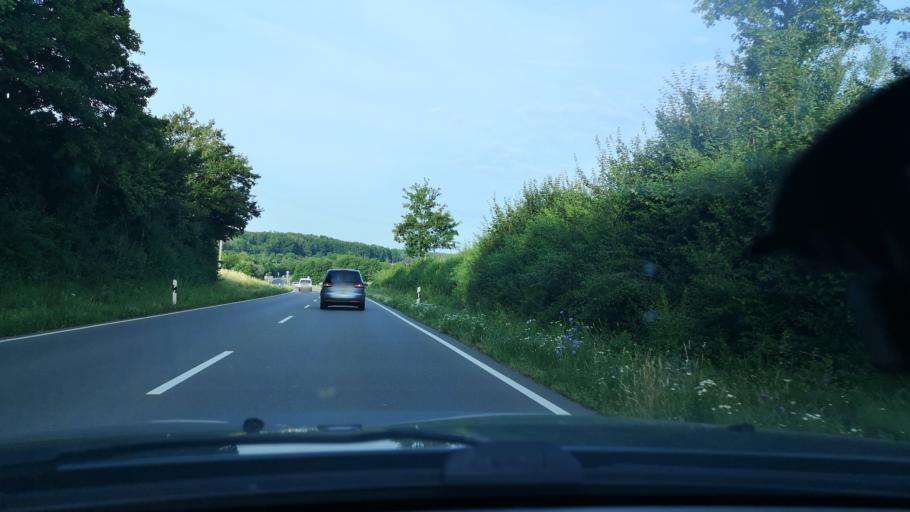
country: DE
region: Baden-Wuerttemberg
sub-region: Regierungsbezirk Stuttgart
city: Schlierbach
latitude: 48.6719
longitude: 9.5087
